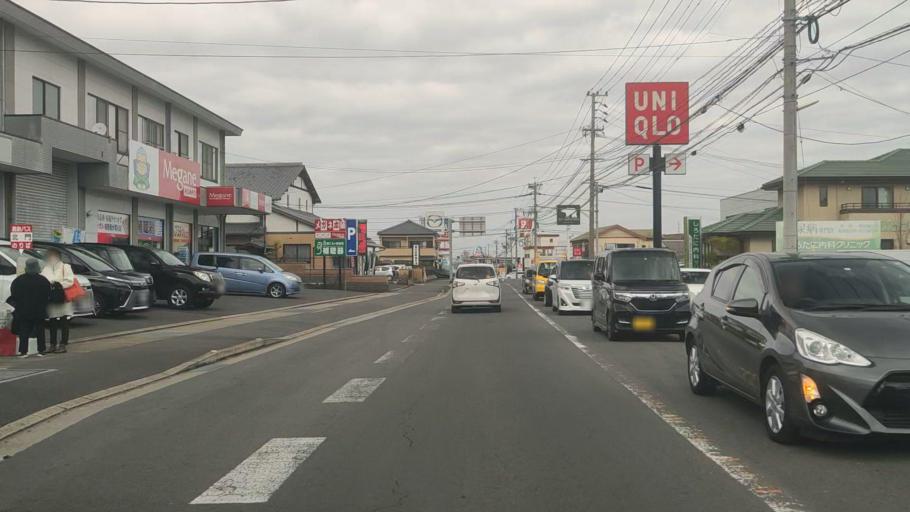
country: JP
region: Nagasaki
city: Shimabara
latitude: 32.8008
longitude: 130.3644
